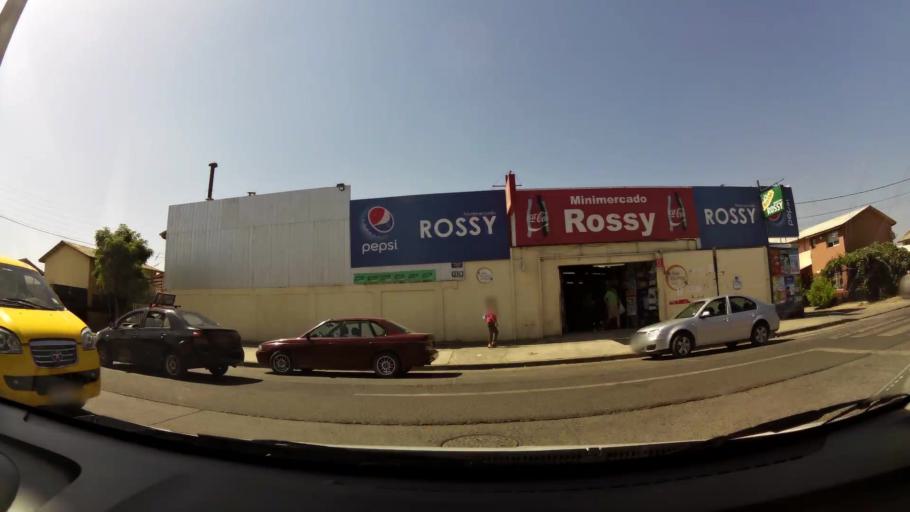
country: CL
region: Maule
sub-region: Provincia de Talca
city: Talca
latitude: -35.4169
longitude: -71.6420
